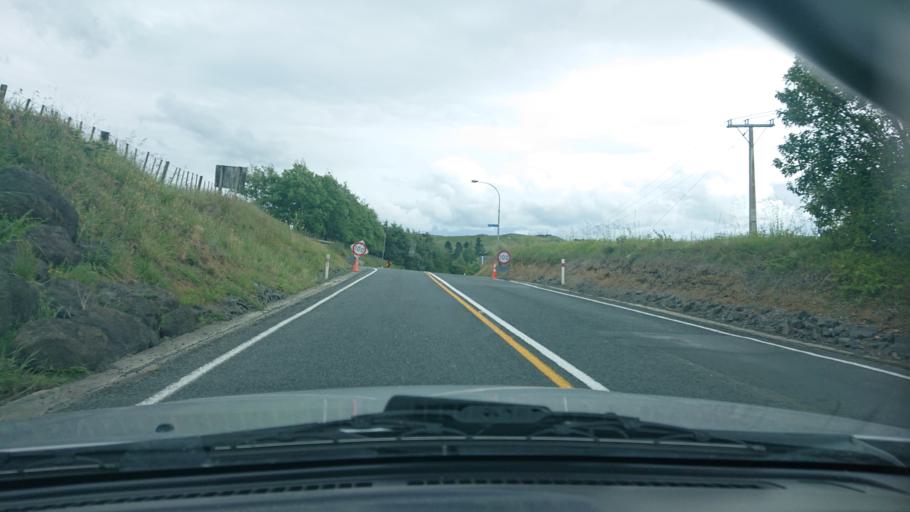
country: NZ
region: Auckland
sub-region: Auckland
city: Wellsford
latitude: -36.3741
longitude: 174.4545
